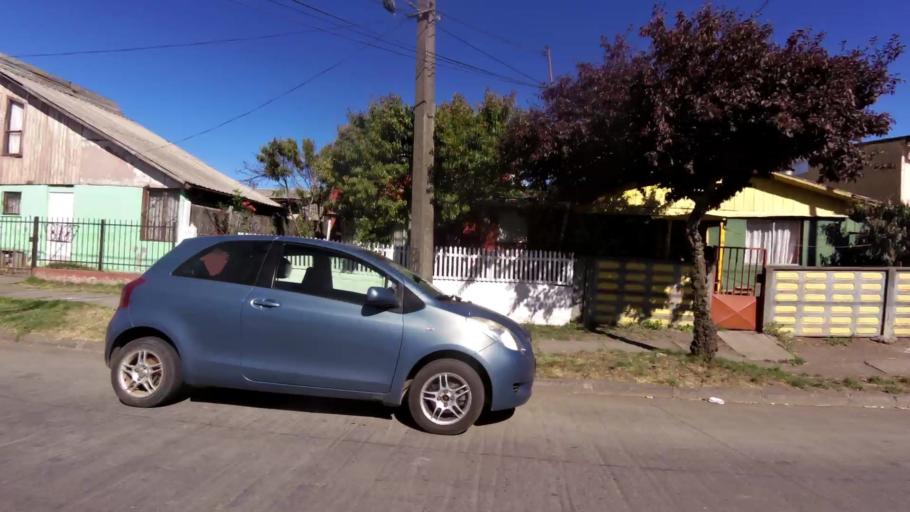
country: CL
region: Biobio
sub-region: Provincia de Concepcion
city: Concepcion
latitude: -36.8155
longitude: -73.0779
